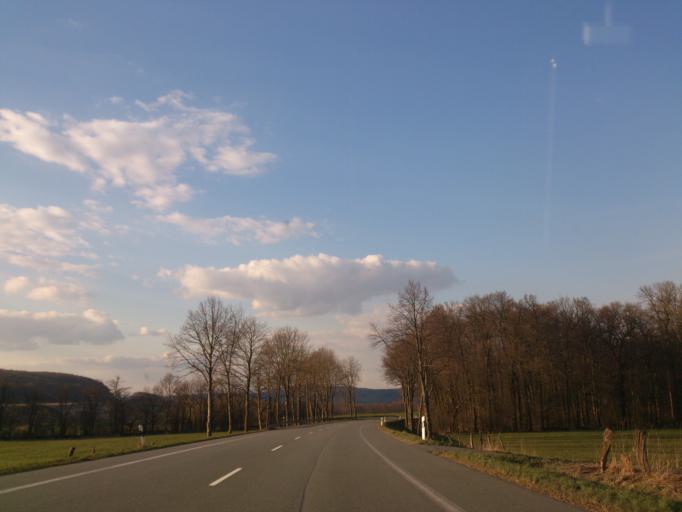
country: DE
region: North Rhine-Westphalia
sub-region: Regierungsbezirk Detmold
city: Willebadessen
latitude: 51.6005
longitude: 9.0320
